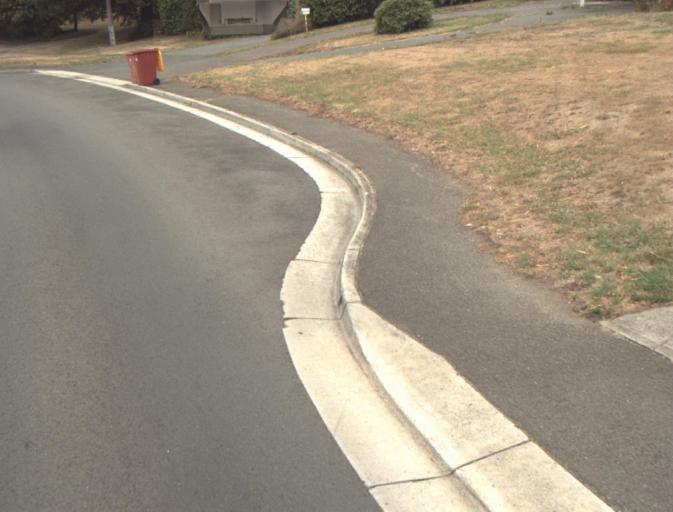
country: AU
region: Tasmania
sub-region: Launceston
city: Summerhill
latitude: -41.4640
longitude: 147.1462
